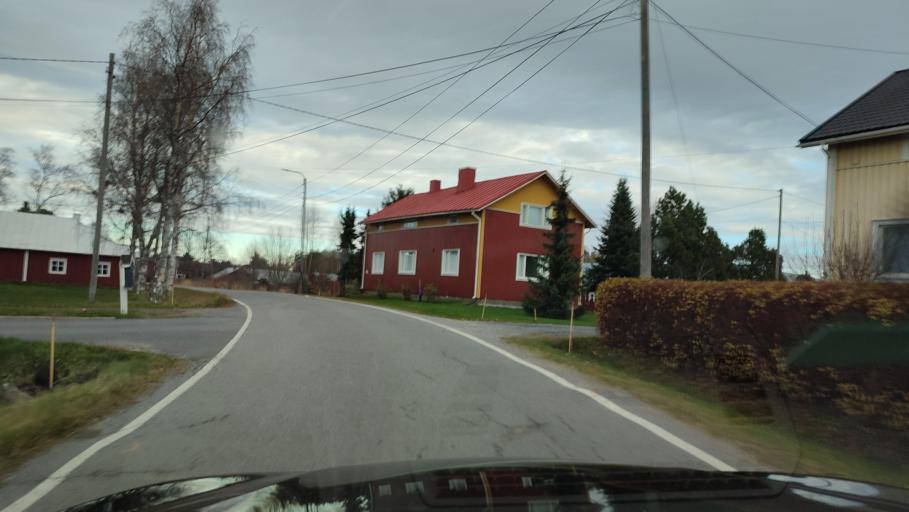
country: FI
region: Ostrobothnia
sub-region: Sydosterbotten
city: Naerpes
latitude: 62.4681
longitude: 21.3716
